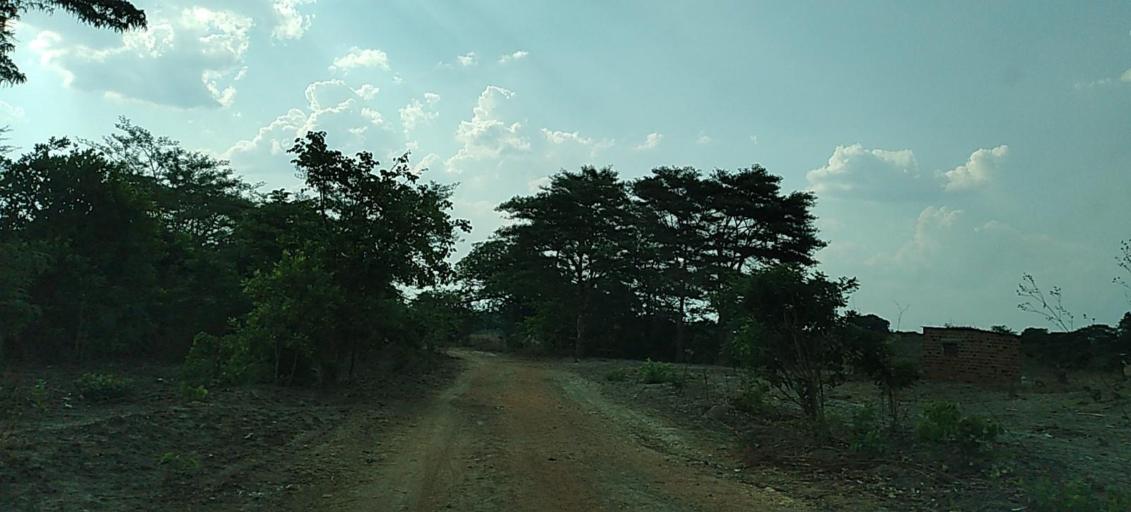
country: ZM
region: Copperbelt
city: Mpongwe
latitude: -13.4764
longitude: 28.0813
